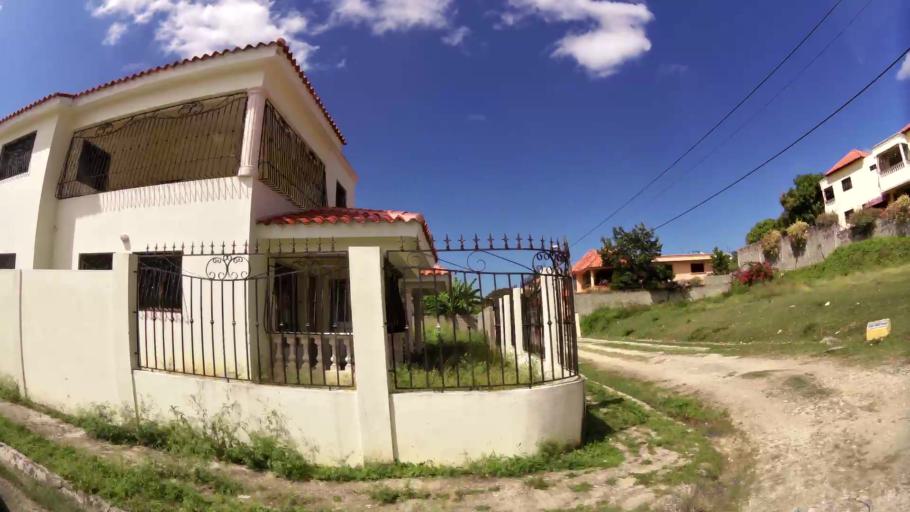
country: DO
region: San Cristobal
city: San Cristobal
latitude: 18.4348
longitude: -70.1293
